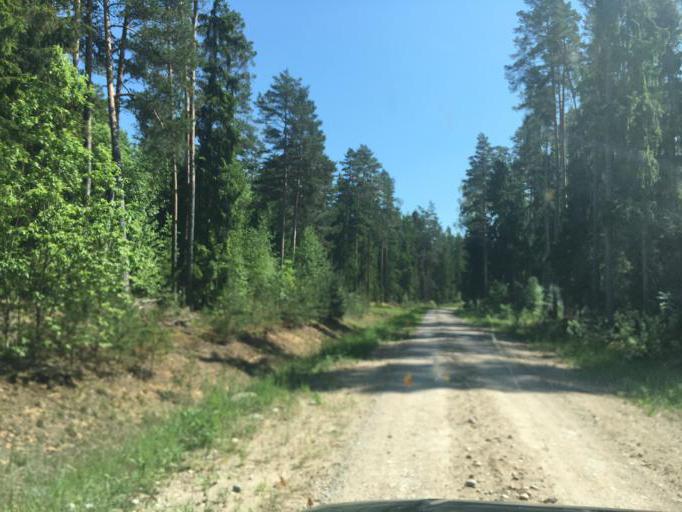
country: LV
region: Talsu Rajons
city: Valdemarpils
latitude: 57.4440
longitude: 22.6621
